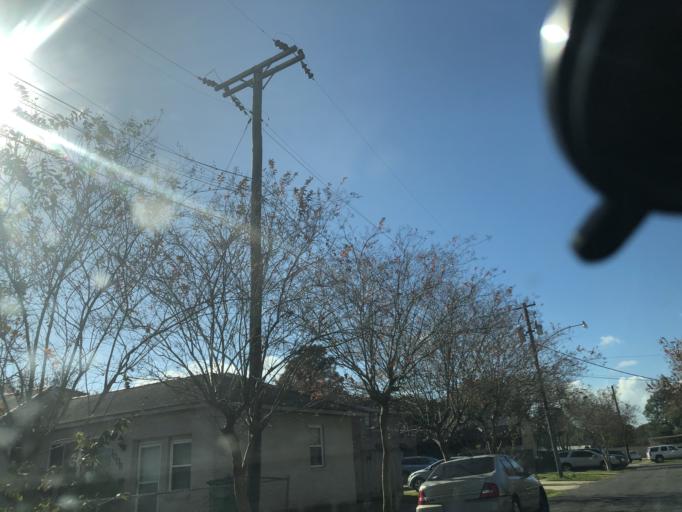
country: US
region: Louisiana
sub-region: Jefferson Parish
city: Metairie Terrace
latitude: 29.9828
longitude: -90.1616
